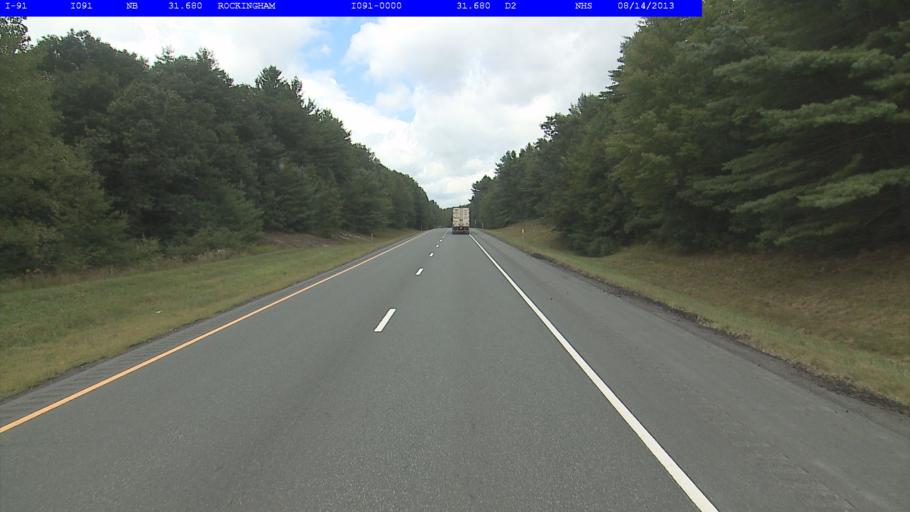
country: US
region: Vermont
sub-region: Windham County
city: Bellows Falls
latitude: 43.1310
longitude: -72.4738
